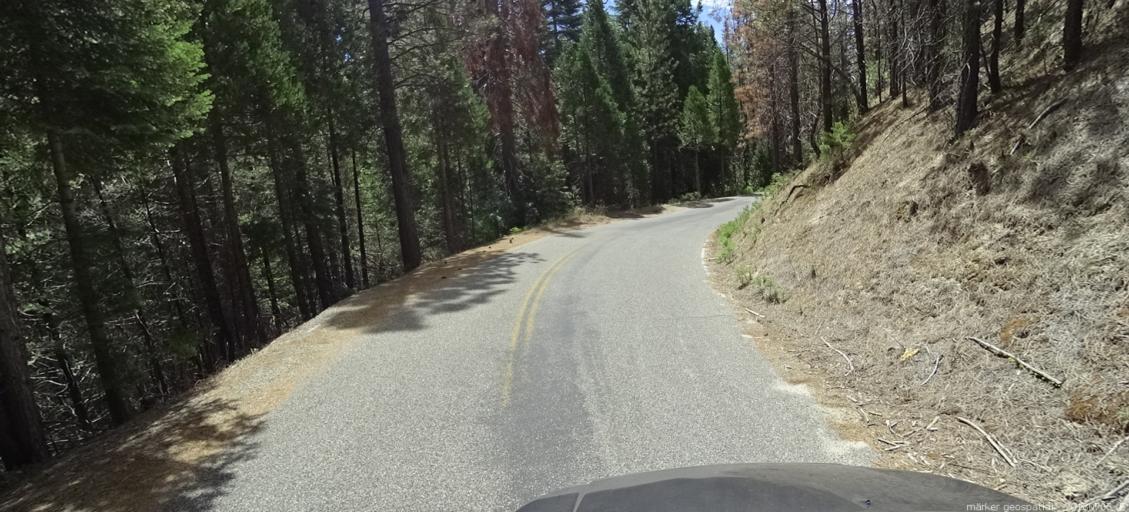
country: US
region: California
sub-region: Madera County
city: Oakhurst
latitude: 37.4073
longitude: -119.3970
